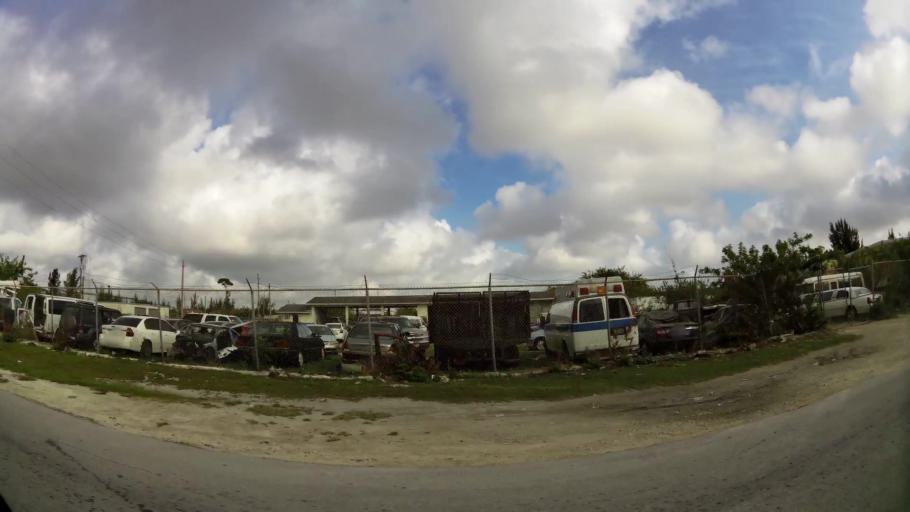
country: BS
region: Freeport
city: Freeport
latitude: 26.5358
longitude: -78.7128
